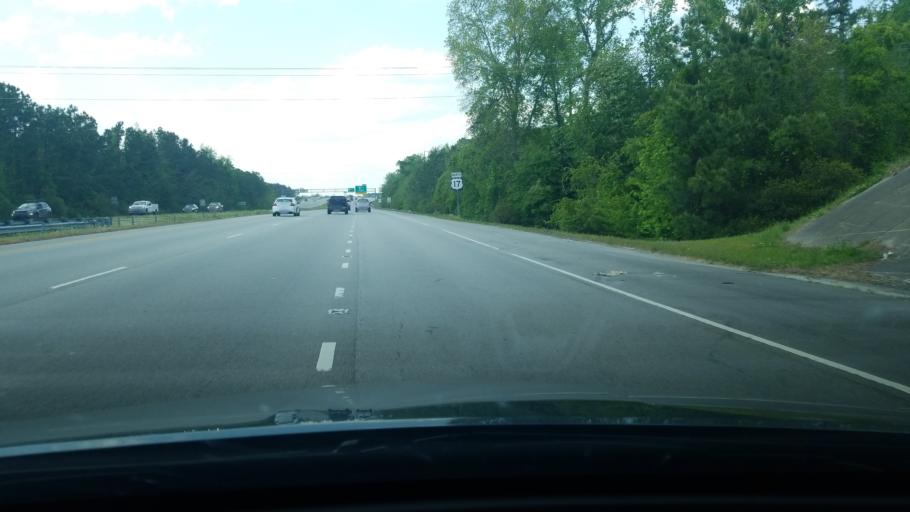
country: US
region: North Carolina
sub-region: Onslow County
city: Pumpkin Center
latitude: 34.7633
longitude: -77.3950
